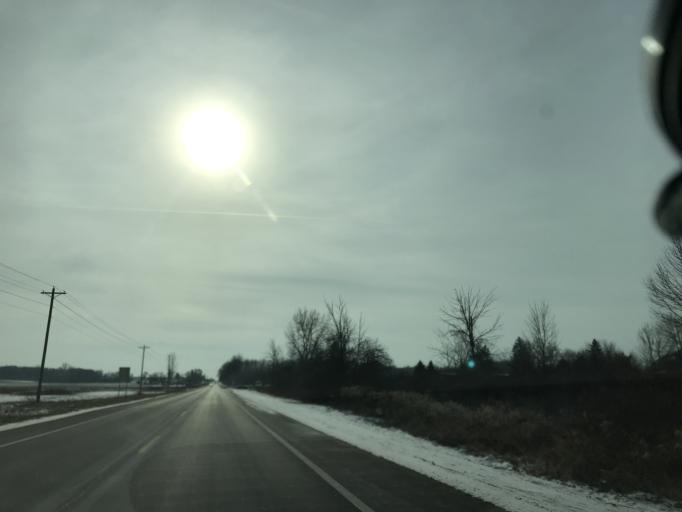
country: US
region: Michigan
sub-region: Ionia County
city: Lake Odessa
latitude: 42.8017
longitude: -85.0745
